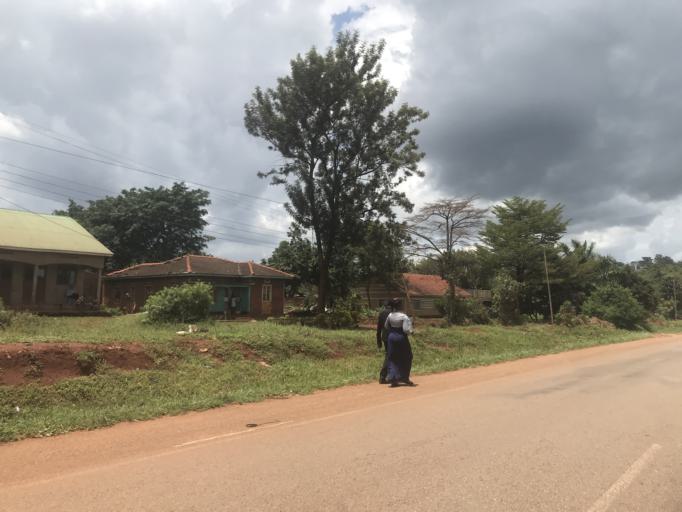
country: UG
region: Eastern Region
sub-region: Jinja District
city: Bugembe
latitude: 0.4764
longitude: 33.2655
